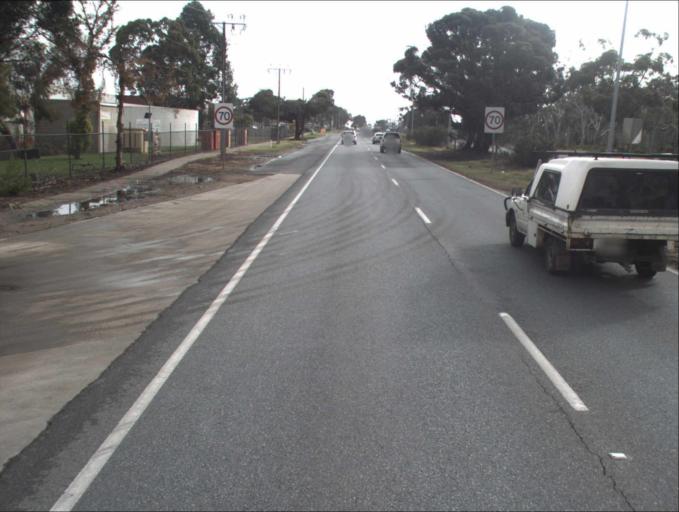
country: AU
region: South Australia
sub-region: Port Adelaide Enfield
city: Enfield
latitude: -34.8412
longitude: 138.5995
